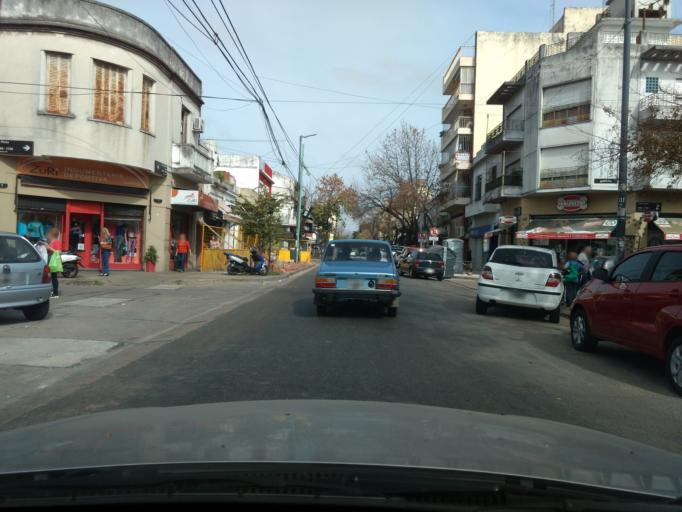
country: AR
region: Buenos Aires F.D.
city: Villa Santa Rita
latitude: -34.6236
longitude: -58.5108
